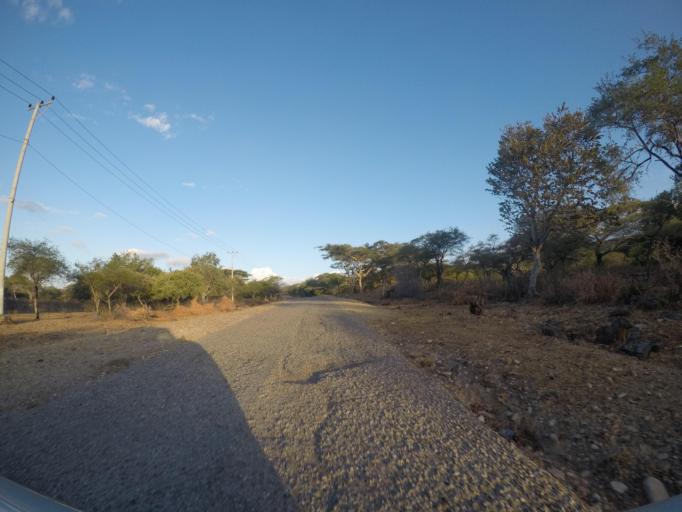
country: TL
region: Lautem
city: Lospalos
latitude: -8.3283
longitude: 126.9991
